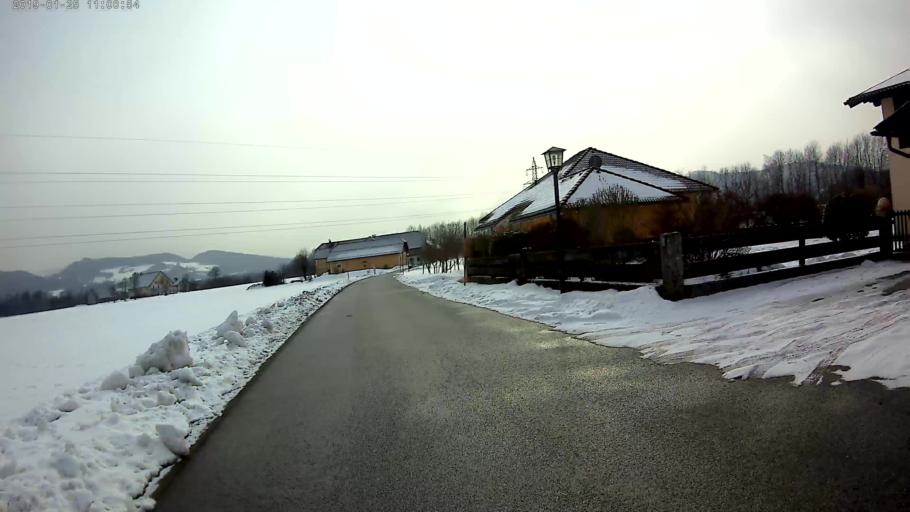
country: AT
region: Salzburg
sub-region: Politischer Bezirk Salzburg-Umgebung
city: Anif
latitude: 47.7405
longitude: 13.0570
